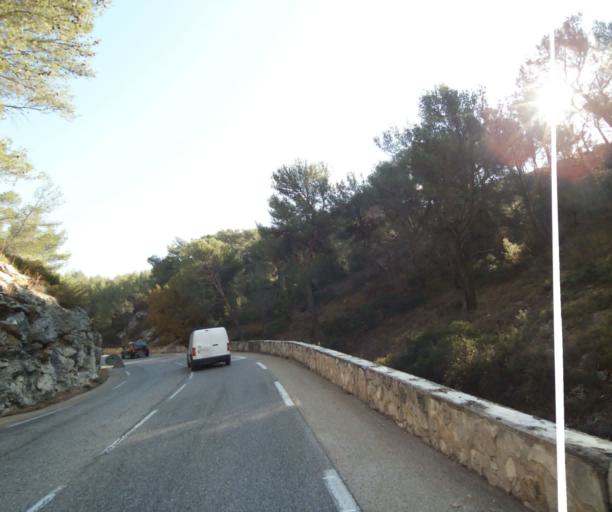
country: FR
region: Provence-Alpes-Cote d'Azur
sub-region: Departement des Bouches-du-Rhone
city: Cadolive
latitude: 43.3686
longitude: 5.5150
